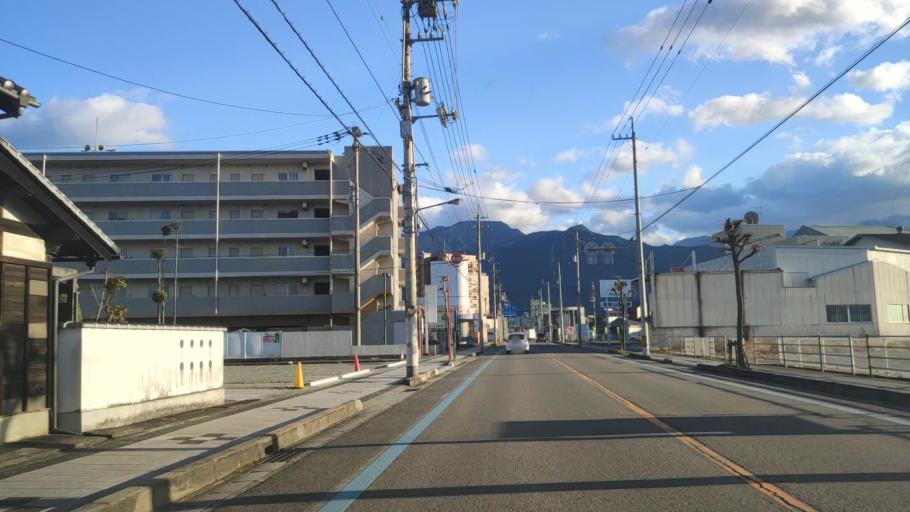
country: JP
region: Ehime
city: Saijo
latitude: 33.9129
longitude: 133.1792
